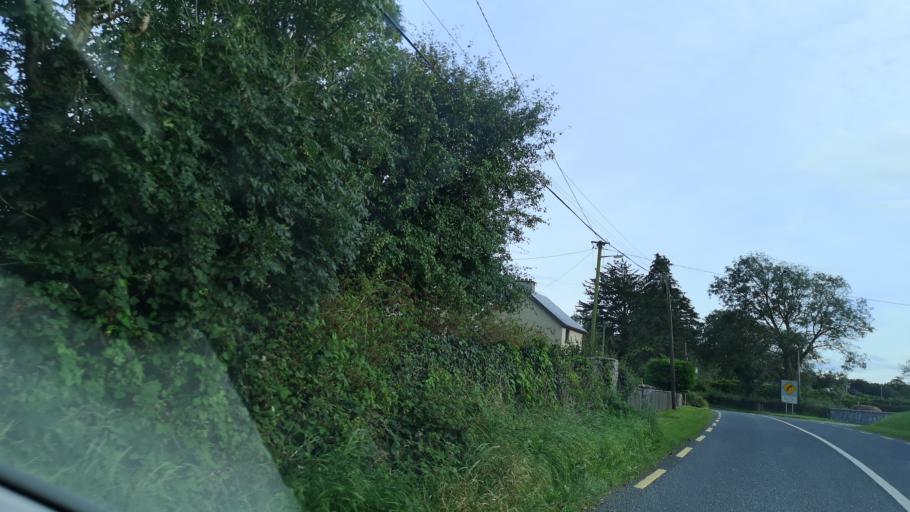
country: IE
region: Connaught
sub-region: County Galway
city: Ballinasloe
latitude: 53.3237
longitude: -8.2796
